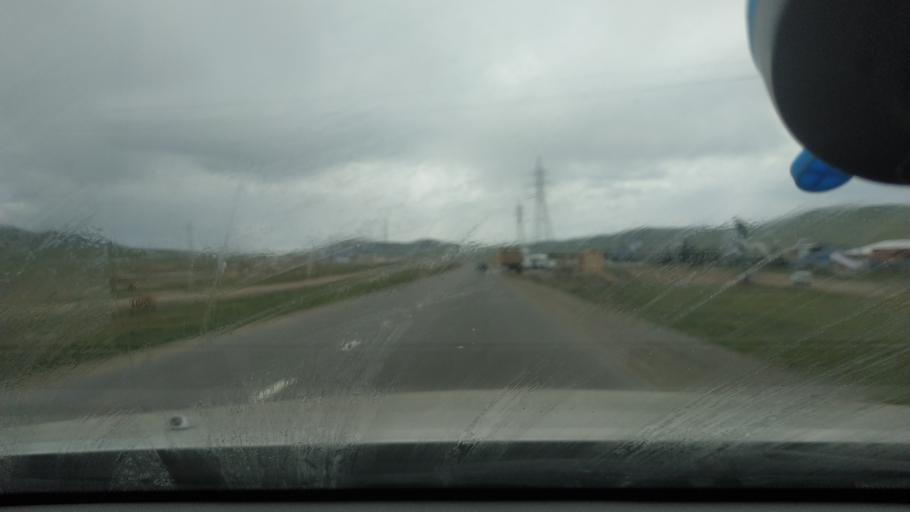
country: MN
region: Ulaanbaatar
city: Ulaanbaatar
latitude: 47.8202
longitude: 106.7604
